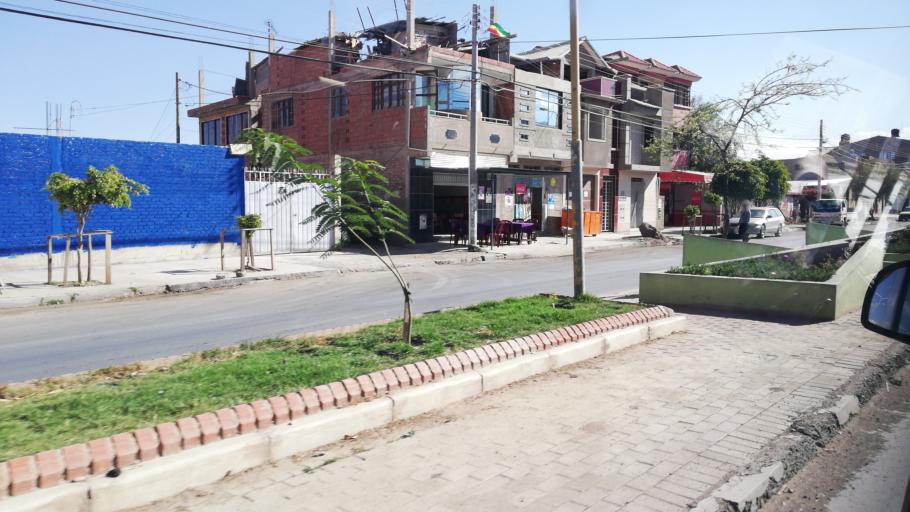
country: BO
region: Cochabamba
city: Cochabamba
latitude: -17.3935
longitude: -66.2500
